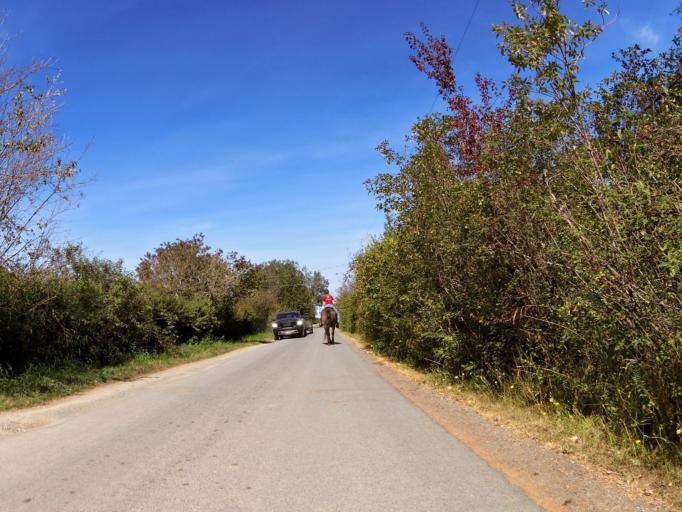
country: CA
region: British Columbia
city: Victoria
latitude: 48.5514
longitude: -123.3858
